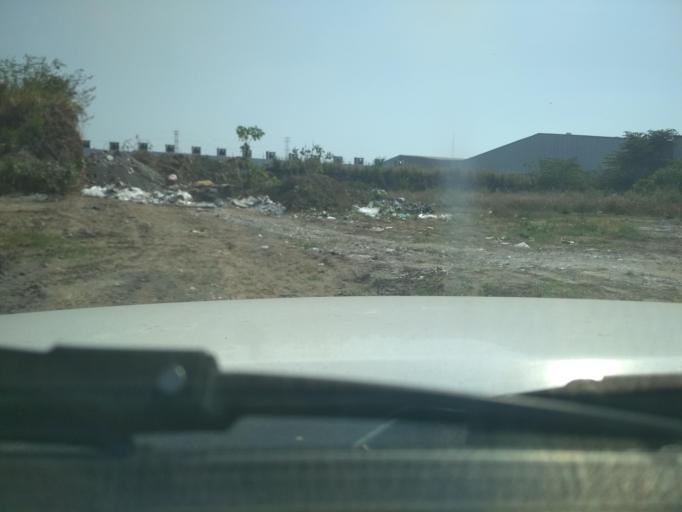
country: MX
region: Veracruz
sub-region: Veracruz
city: Las Amapolas
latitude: 19.1585
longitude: -96.2240
